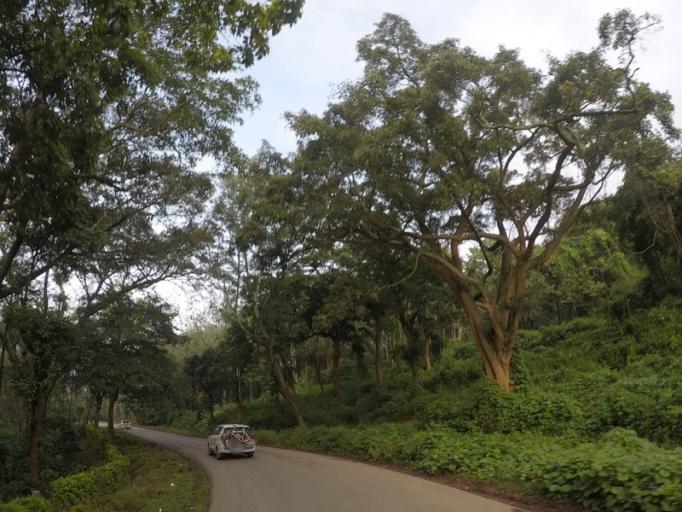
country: IN
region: Karnataka
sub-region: Chikmagalur
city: Chikmagalur
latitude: 13.4571
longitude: 75.7990
